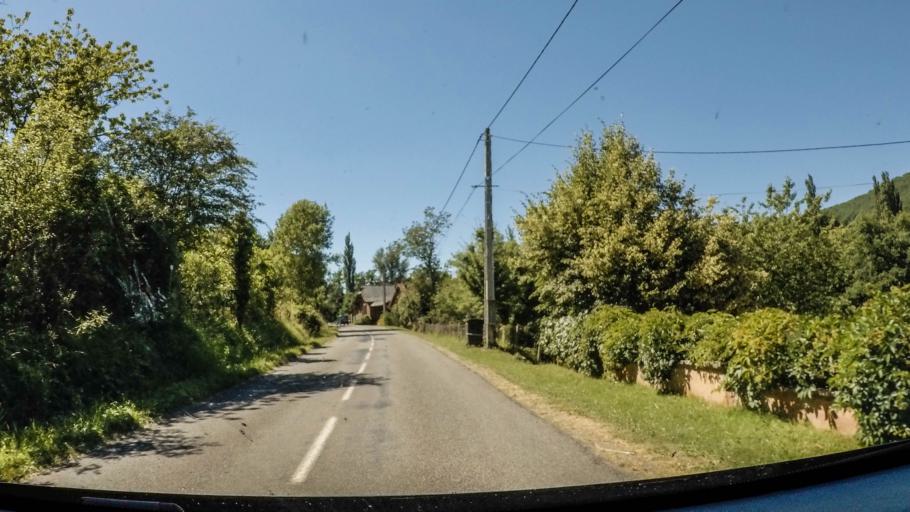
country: FR
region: Midi-Pyrenees
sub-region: Departement de l'Aveyron
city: Saint-Christophe-Vallon
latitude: 44.4654
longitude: 2.3791
